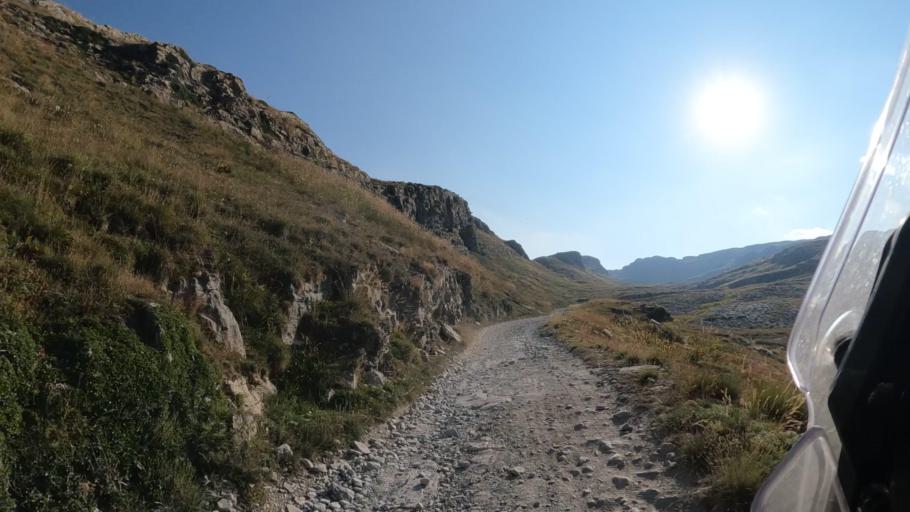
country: IT
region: Piedmont
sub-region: Provincia di Cuneo
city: Limone Piemonte
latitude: 44.1718
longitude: 7.6432
